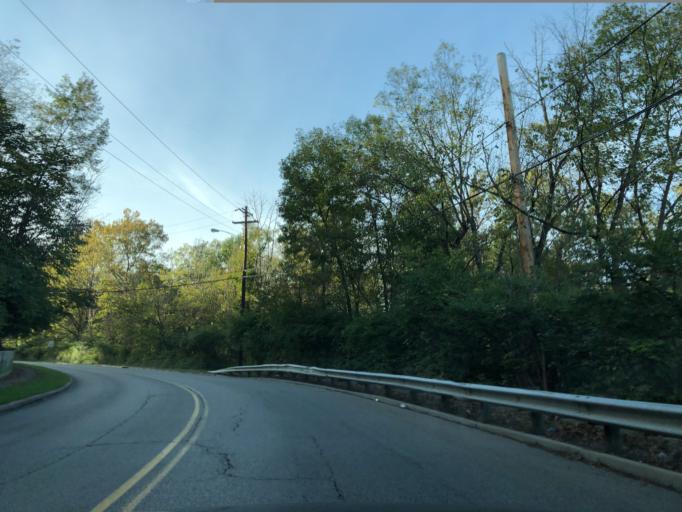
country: US
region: Ohio
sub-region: Hamilton County
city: Loveland
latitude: 39.2696
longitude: -84.2677
